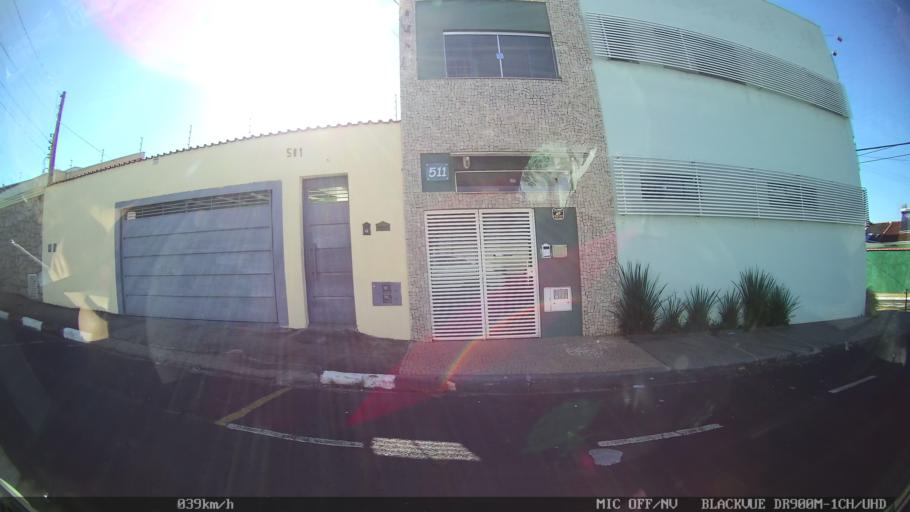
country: BR
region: Sao Paulo
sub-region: Franca
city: Franca
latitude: -20.5409
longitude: -47.4126
